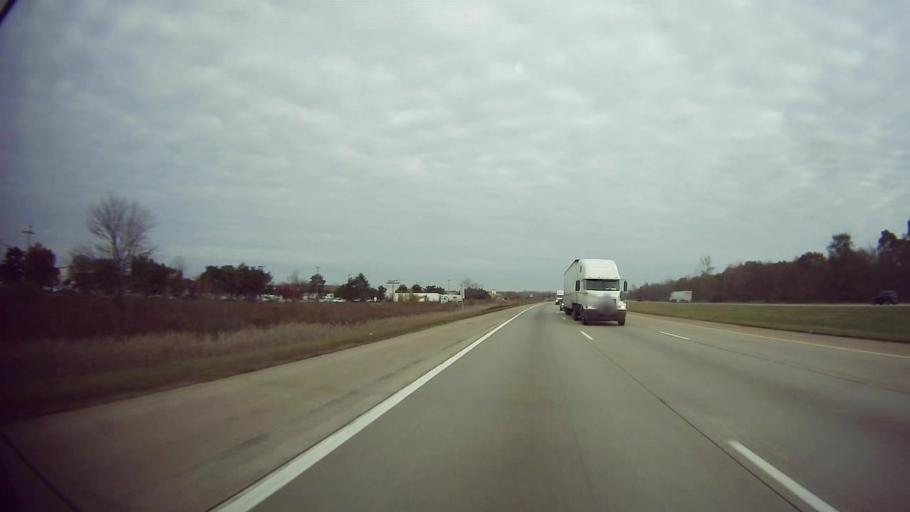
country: US
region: Michigan
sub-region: Monroe County
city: Carleton
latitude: 42.1272
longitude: -83.3817
